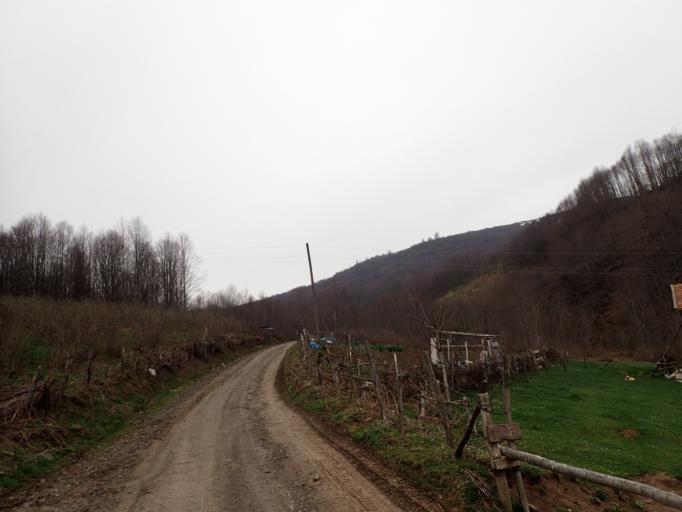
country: TR
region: Ordu
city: Kumru
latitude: 40.7836
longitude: 37.1891
